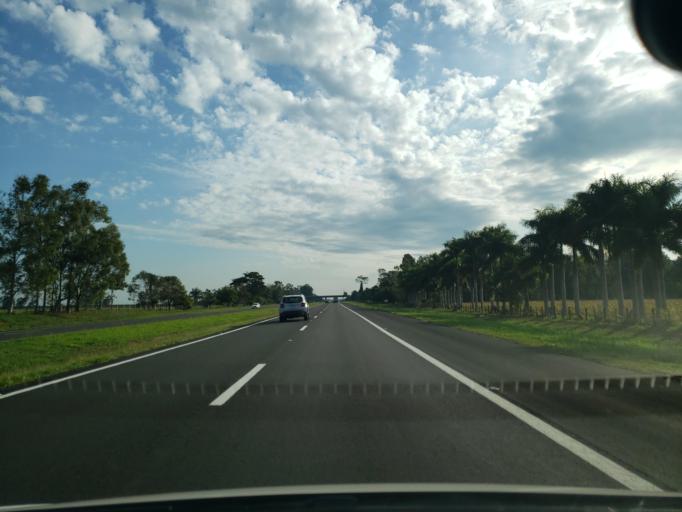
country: BR
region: Sao Paulo
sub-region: Guararapes
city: Guararapes
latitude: -21.2036
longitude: -50.6098
